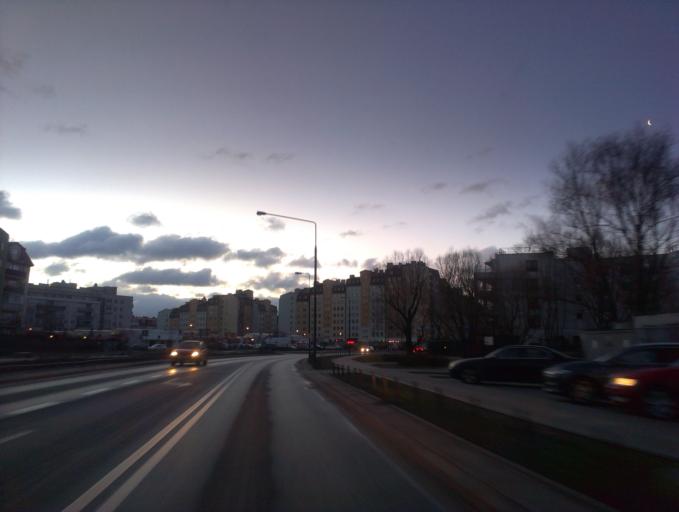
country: PL
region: Masovian Voivodeship
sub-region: Warszawa
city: Ursynow
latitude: 52.1329
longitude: 21.0549
